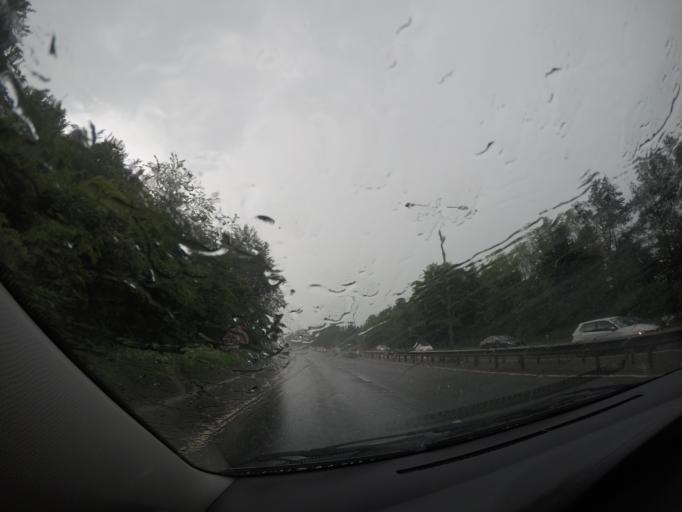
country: GB
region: England
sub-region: Cumbria
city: Penrith
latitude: 54.6523
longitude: -2.7628
